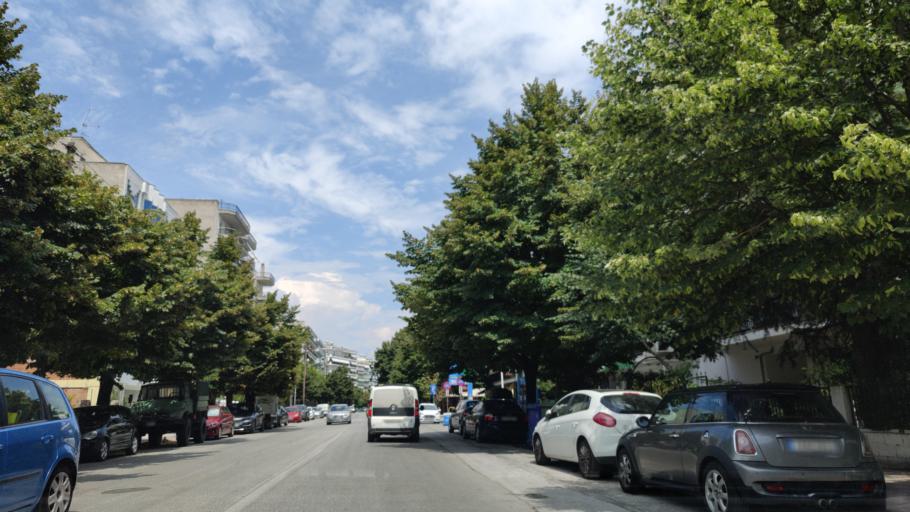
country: GR
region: Central Macedonia
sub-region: Nomos Serron
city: Serres
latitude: 41.0835
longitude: 23.5435
